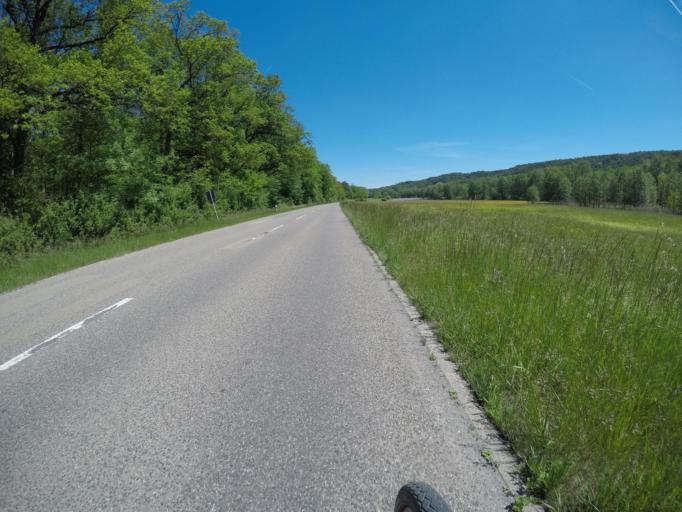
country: DE
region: Baden-Wuerttemberg
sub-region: Regierungsbezirk Stuttgart
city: Magstadt
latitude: 48.7425
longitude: 9.0031
